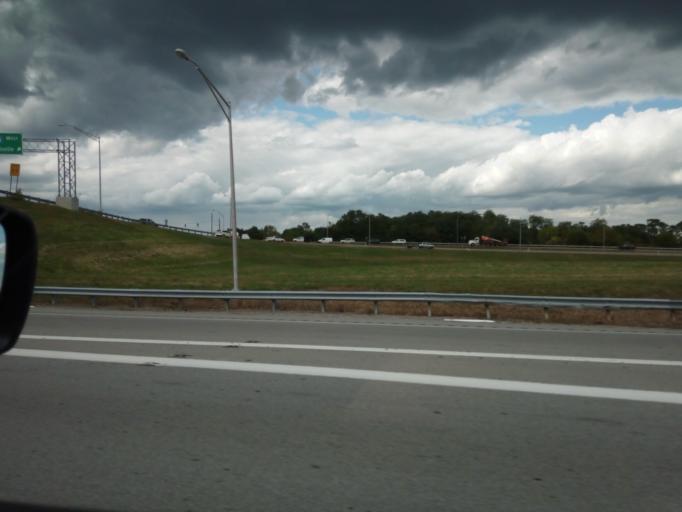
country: US
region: Kentucky
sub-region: Jefferson County
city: Douglass Hills
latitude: 38.2239
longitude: -85.5385
